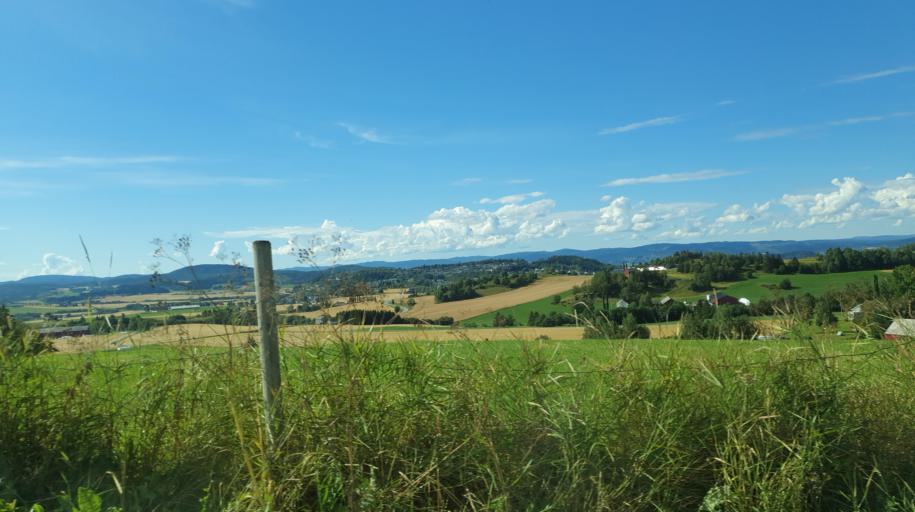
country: NO
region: Nord-Trondelag
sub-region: Levanger
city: Skogn
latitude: 63.6950
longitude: 11.2350
